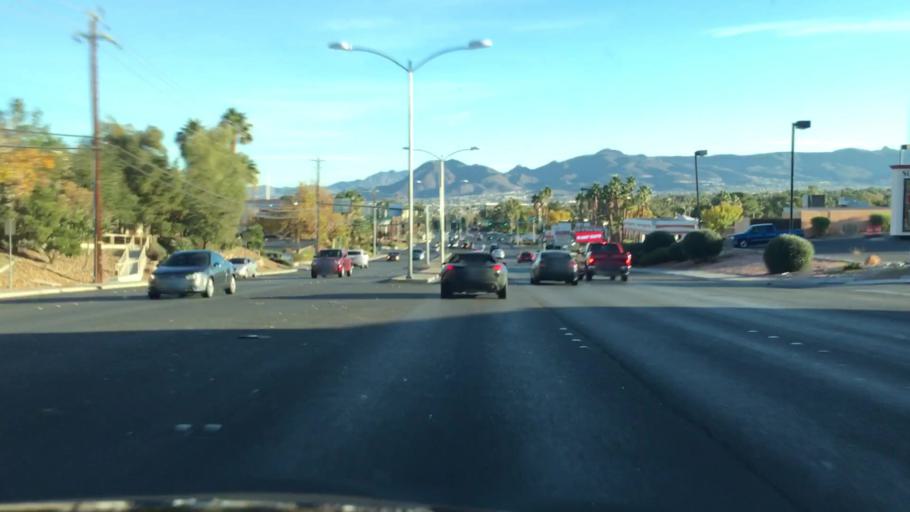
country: US
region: Nevada
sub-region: Clark County
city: Whitney
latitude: 36.0694
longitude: -115.0696
